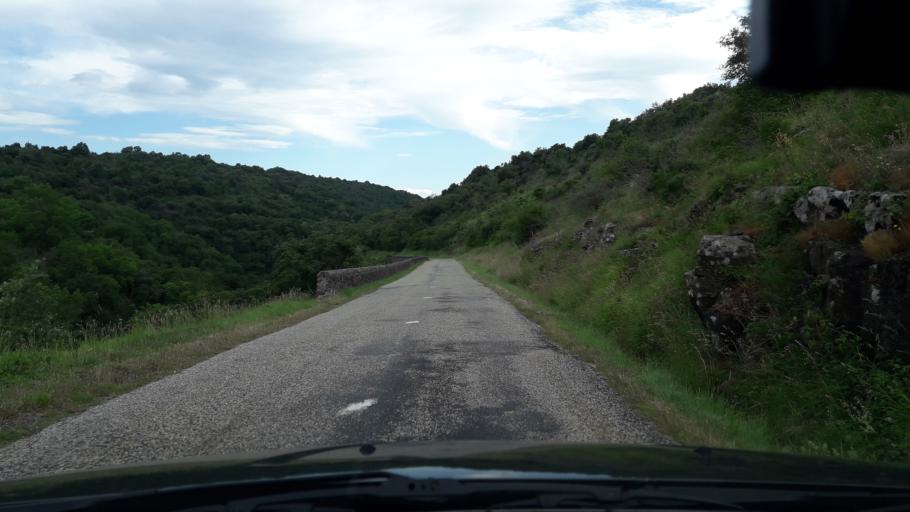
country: FR
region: Rhone-Alpes
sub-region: Departement de l'Ardeche
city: Saint-Priest
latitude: 44.6630
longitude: 4.5308
